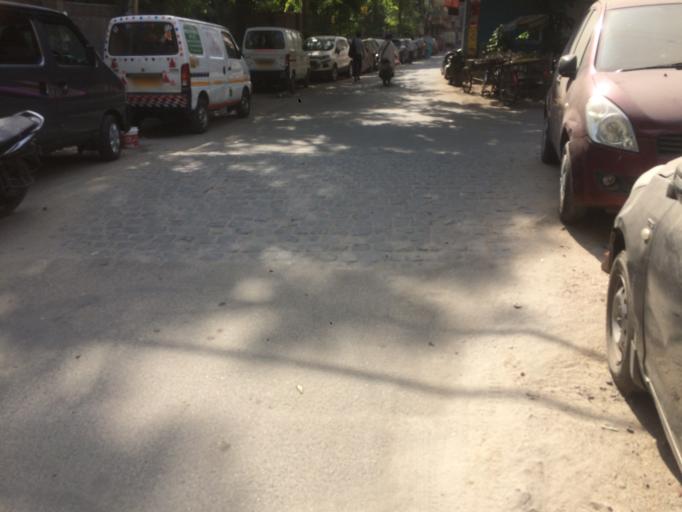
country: IN
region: NCT
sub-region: New Delhi
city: New Delhi
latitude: 28.5798
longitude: 77.2567
